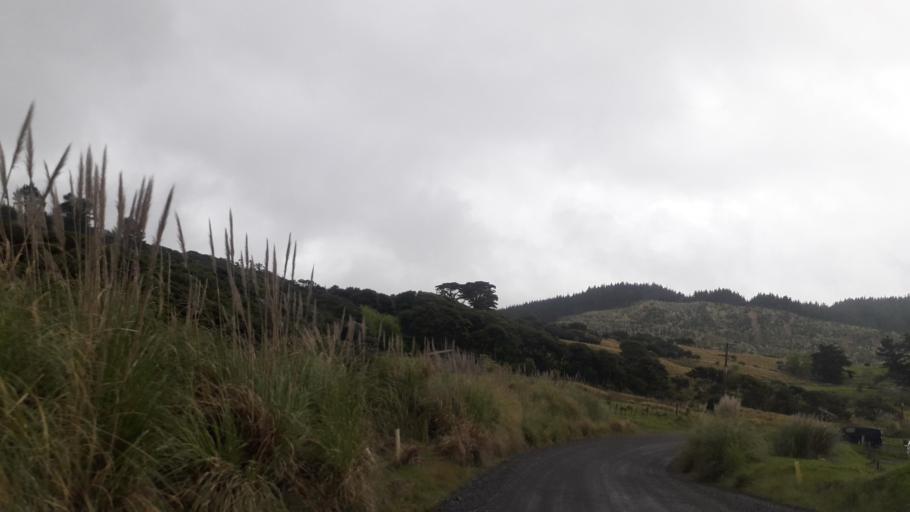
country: NZ
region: Northland
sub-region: Far North District
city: Ahipara
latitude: -35.4359
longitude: 173.3318
